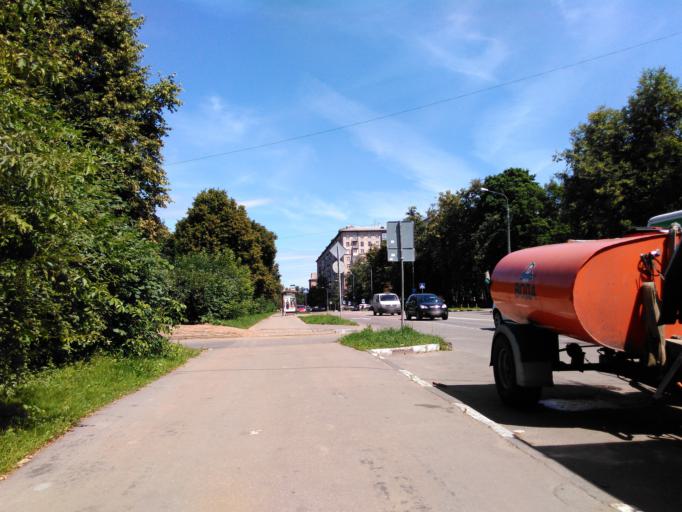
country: RU
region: Moskovskaya
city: Semenovskoye
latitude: 55.6954
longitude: 37.5442
